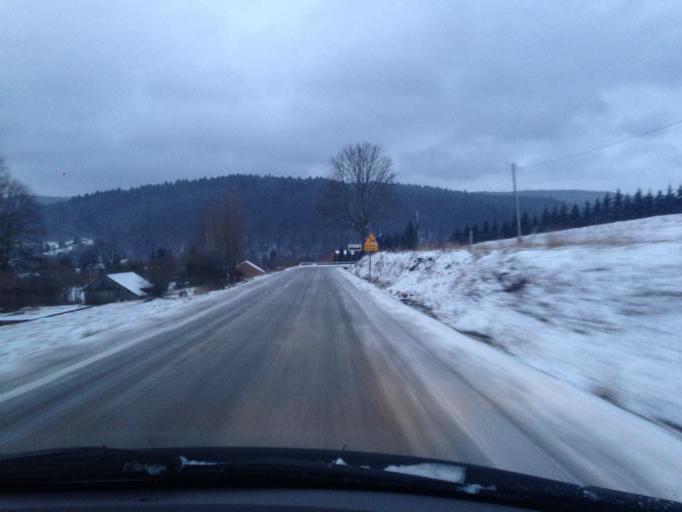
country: PL
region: Subcarpathian Voivodeship
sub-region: Powiat jasielski
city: Krempna
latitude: 49.5145
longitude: 21.5025
